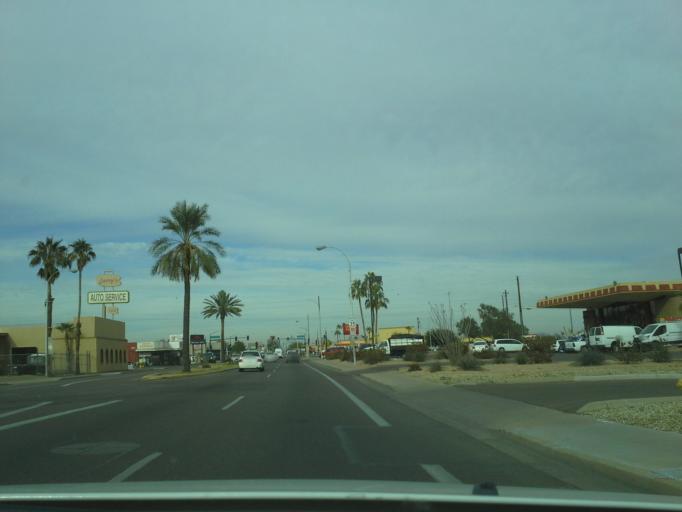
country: US
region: Arizona
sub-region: Maricopa County
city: Phoenix
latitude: 33.4046
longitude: -112.0733
